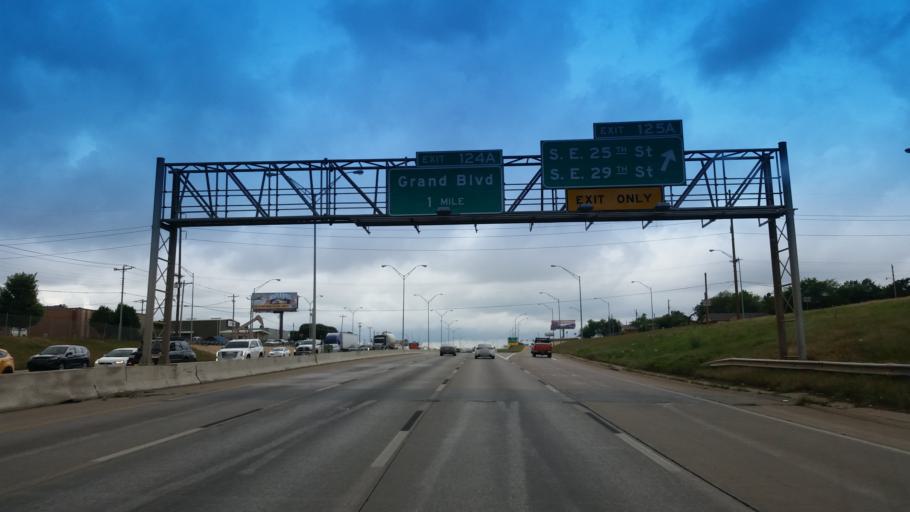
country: US
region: Oklahoma
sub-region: Oklahoma County
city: Oklahoma City
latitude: 35.4441
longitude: -97.4863
